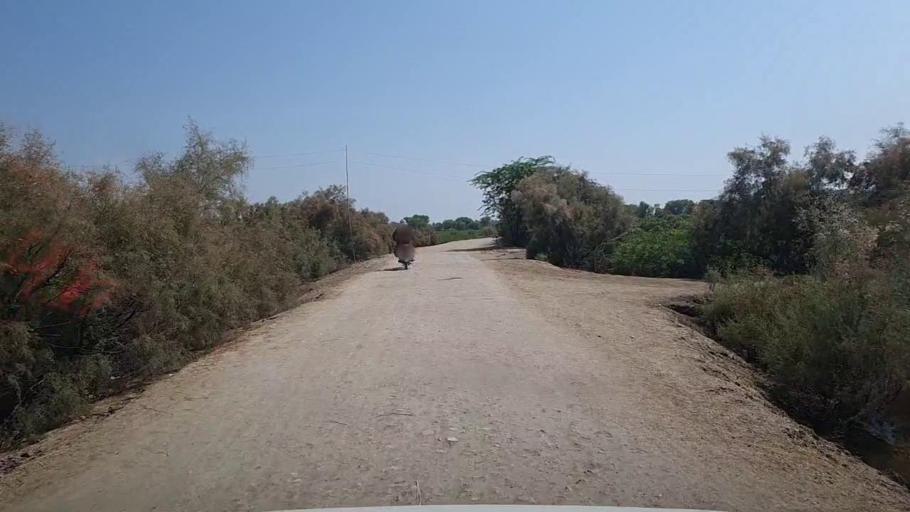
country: PK
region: Sindh
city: Kandhkot
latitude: 28.2742
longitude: 69.3593
